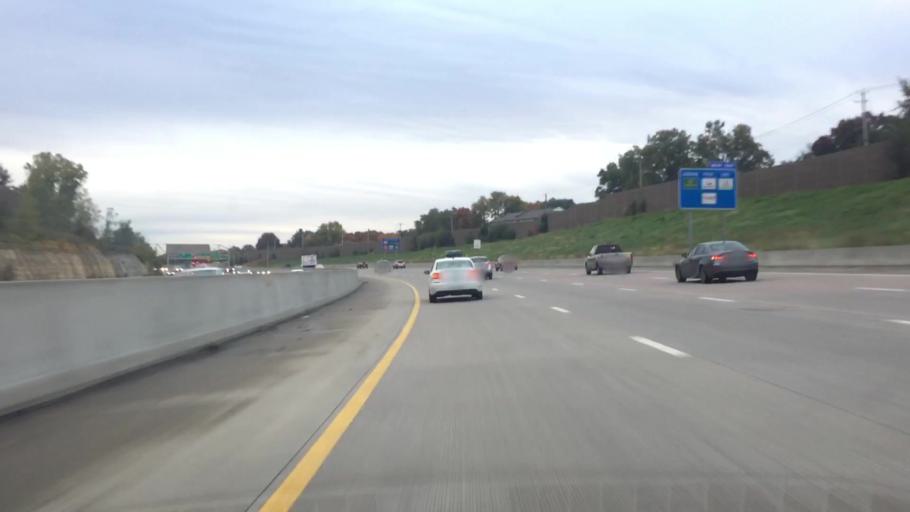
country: US
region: Kansas
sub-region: Johnson County
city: Lenexa
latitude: 38.9629
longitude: -94.7136
